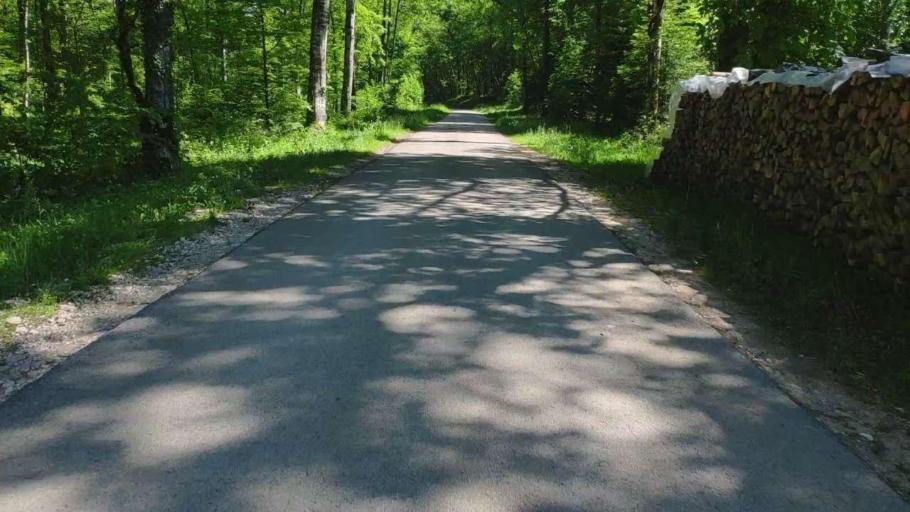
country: FR
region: Franche-Comte
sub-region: Departement du Jura
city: Poligny
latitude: 46.7478
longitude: 5.7758
